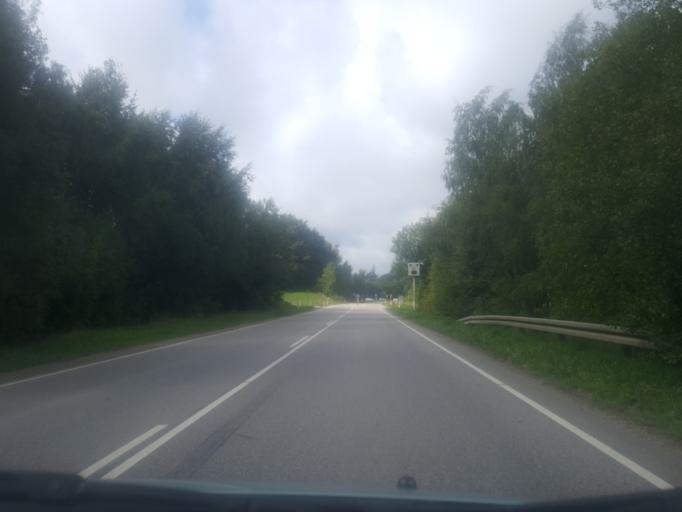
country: DK
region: Zealand
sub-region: Soro Kommune
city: Soro
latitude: 55.4658
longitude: 11.5553
